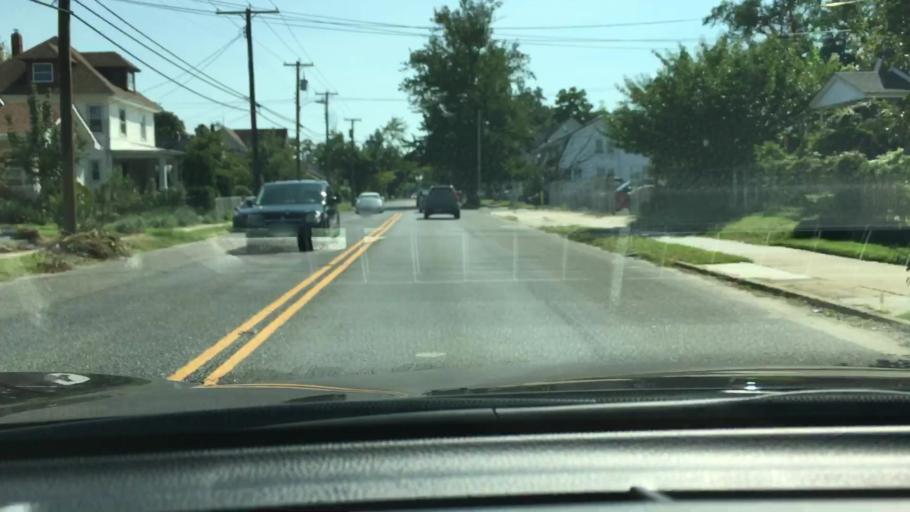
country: US
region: New Jersey
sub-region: Cumberland County
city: Millville
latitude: 39.3952
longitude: -75.0294
